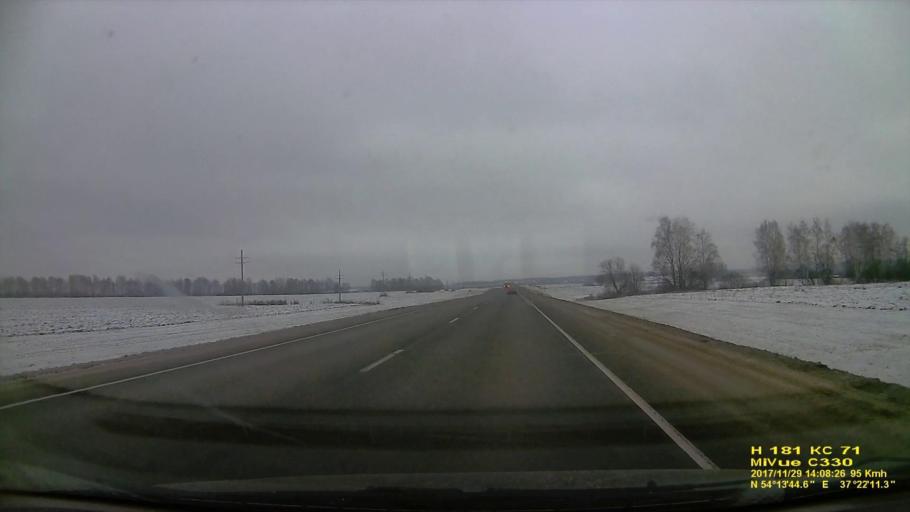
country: RU
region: Tula
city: Leninskiy
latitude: 54.2289
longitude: 37.3702
